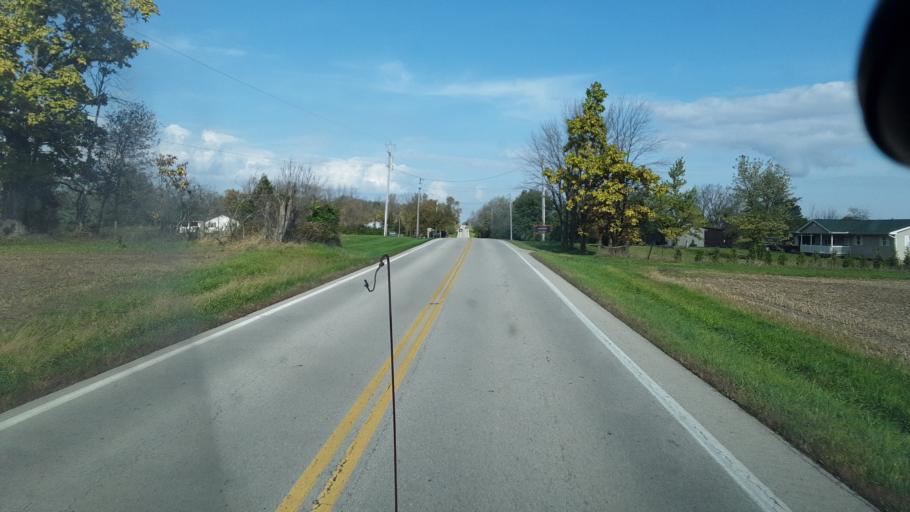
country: US
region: Ohio
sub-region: Clinton County
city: Sabina
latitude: 39.5102
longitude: -83.6886
